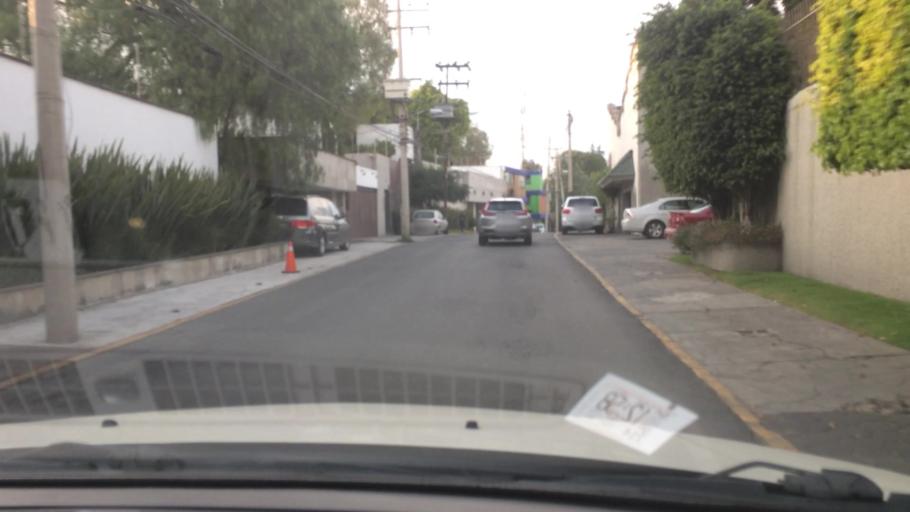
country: MX
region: Mexico City
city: Magdalena Contreras
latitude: 19.3230
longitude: -99.2122
